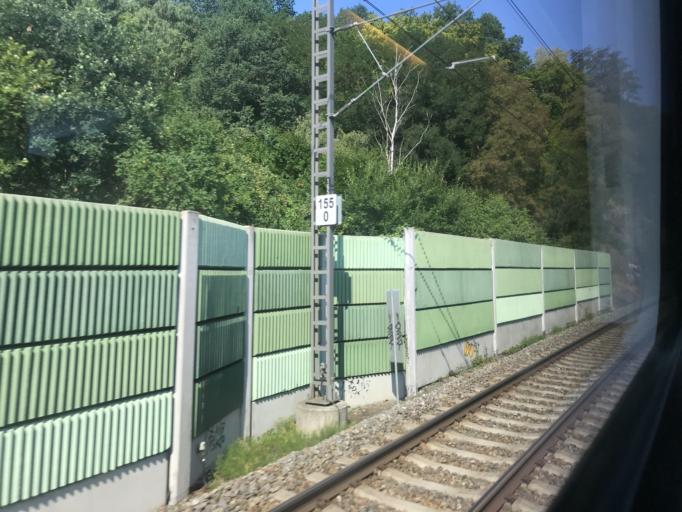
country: CZ
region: Central Bohemia
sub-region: Okres Praha-Vychod
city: Mnichovice
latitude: 49.9346
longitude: 14.7042
